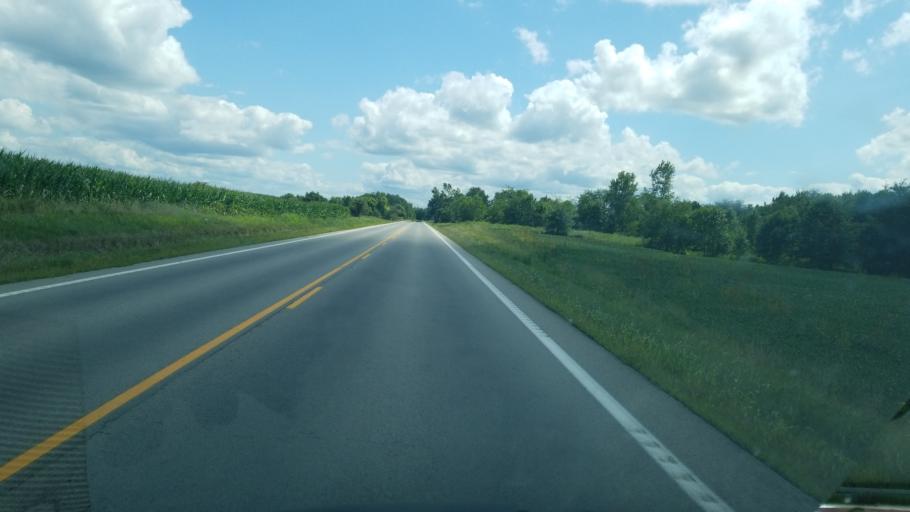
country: US
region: Ohio
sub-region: Putnam County
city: Kalida
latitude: 40.9449
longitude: -84.1612
